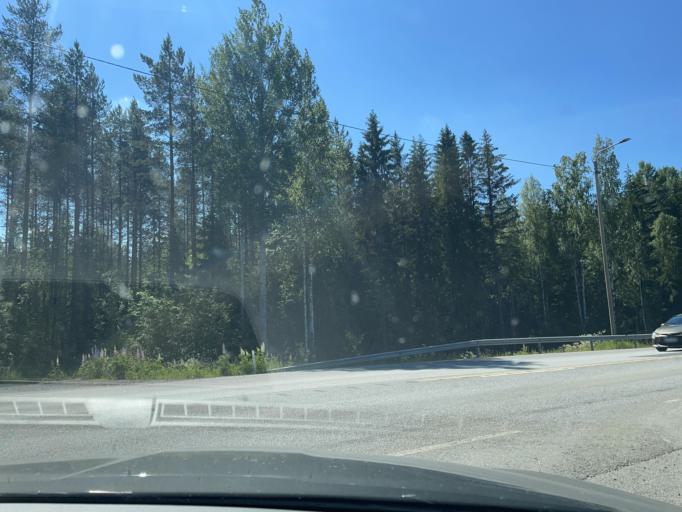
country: FI
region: Central Finland
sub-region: Saarijaervi-Viitasaari
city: Viitasaari
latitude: 63.1783
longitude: 26.0329
